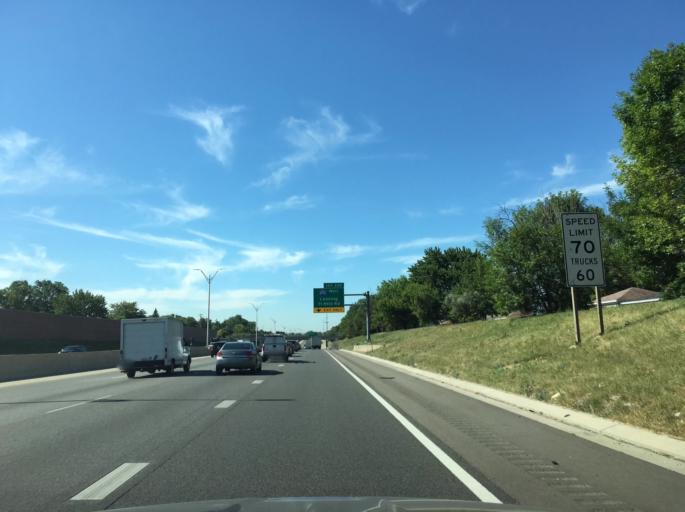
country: US
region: Michigan
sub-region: Macomb County
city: Roseville
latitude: 42.5058
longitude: -82.9183
